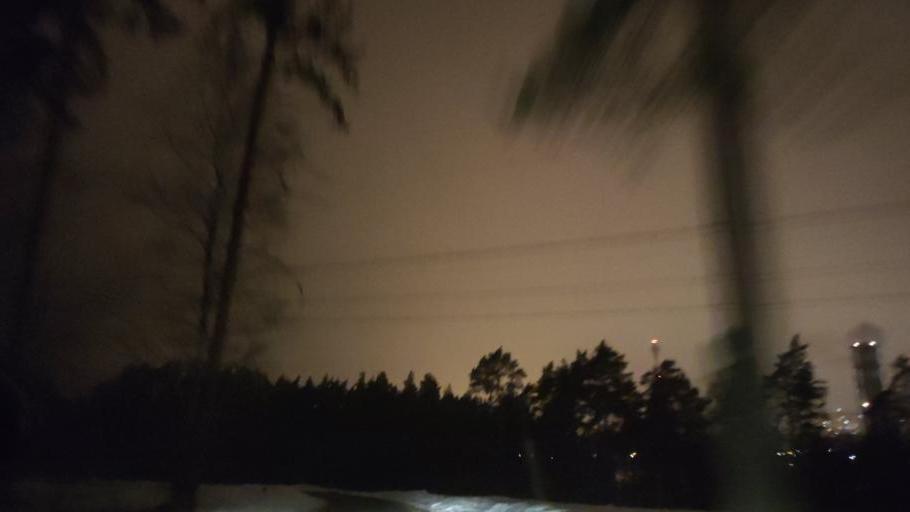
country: RU
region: Moscow
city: Zagor'ye
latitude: 55.5254
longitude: 37.6322
